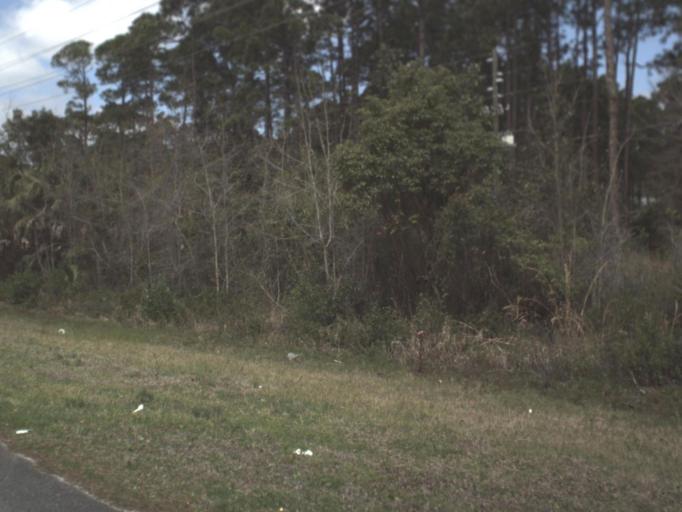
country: US
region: Florida
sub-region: Franklin County
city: Apalachicola
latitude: 29.7148
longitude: -85.0267
